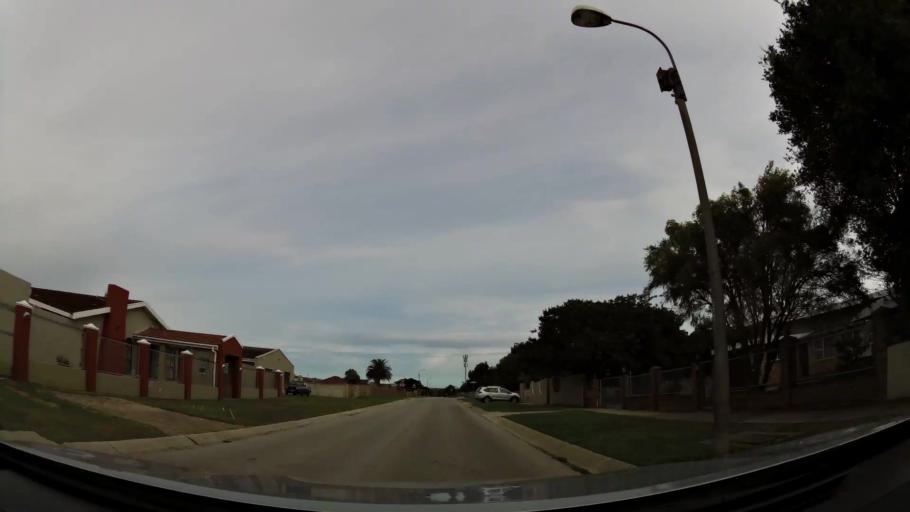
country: ZA
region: Eastern Cape
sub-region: Nelson Mandela Bay Metropolitan Municipality
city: Port Elizabeth
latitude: -33.9421
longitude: 25.4954
